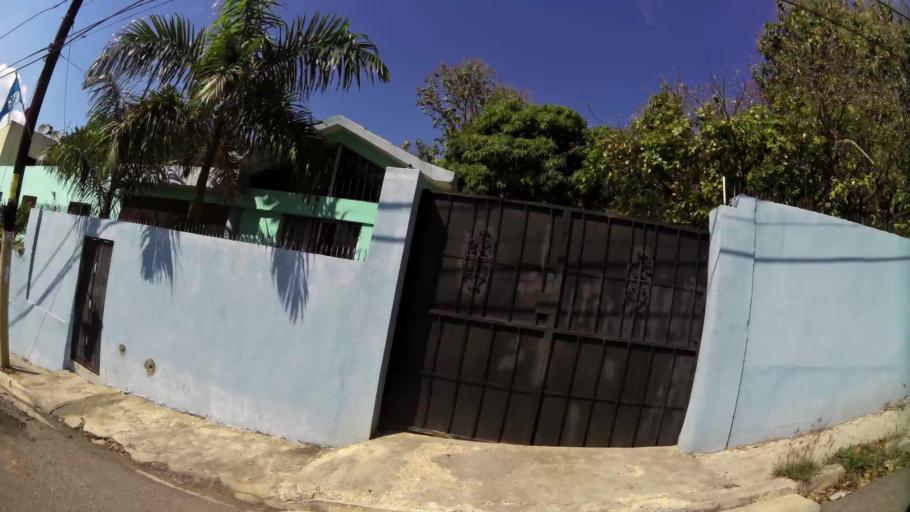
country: DO
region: Santo Domingo
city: Santo Domingo Oeste
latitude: 18.4727
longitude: -70.0062
